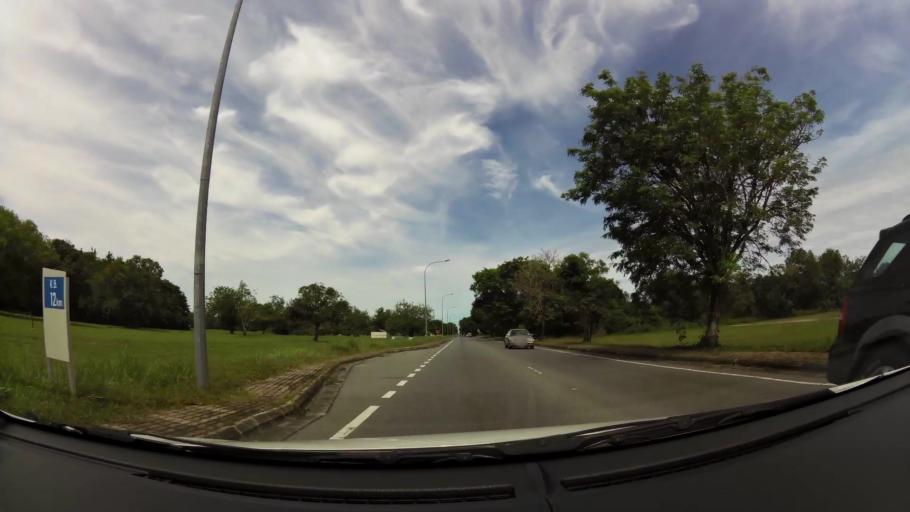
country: BN
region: Belait
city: Seria
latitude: 4.6049
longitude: 114.2979
